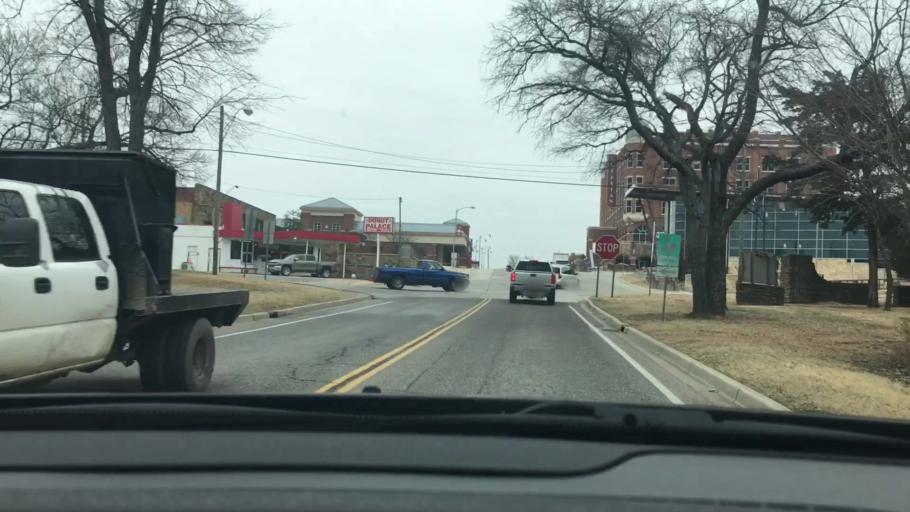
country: US
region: Oklahoma
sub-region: Murray County
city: Sulphur
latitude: 34.5059
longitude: -96.9690
